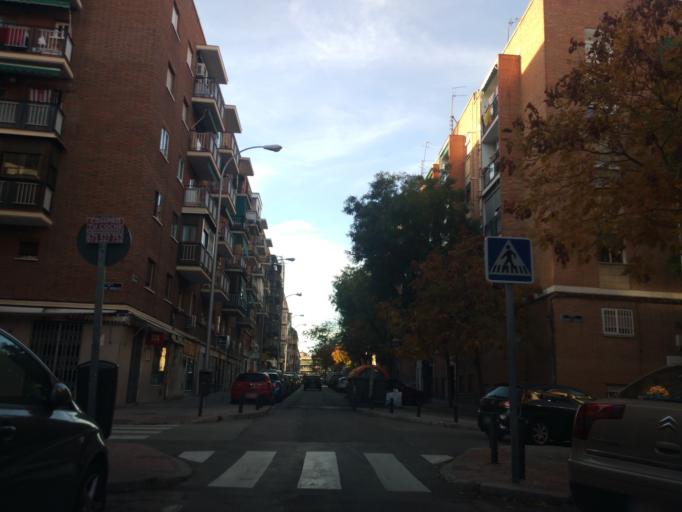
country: ES
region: Madrid
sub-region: Provincia de Madrid
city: Latina
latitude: 40.3871
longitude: -3.7374
